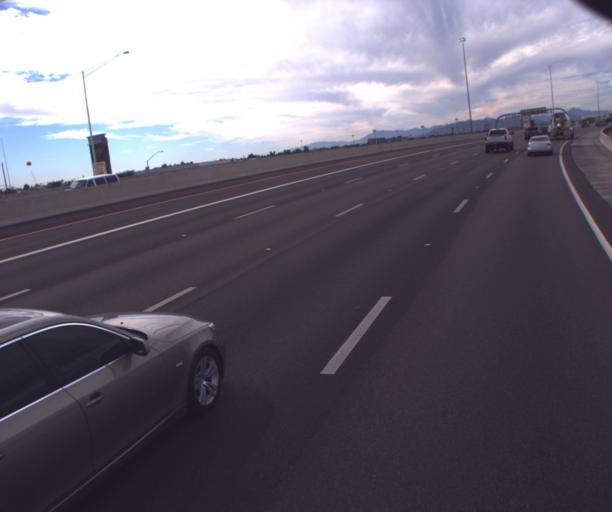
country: US
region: Arizona
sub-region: Maricopa County
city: Tempe
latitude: 33.4380
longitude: -111.8694
